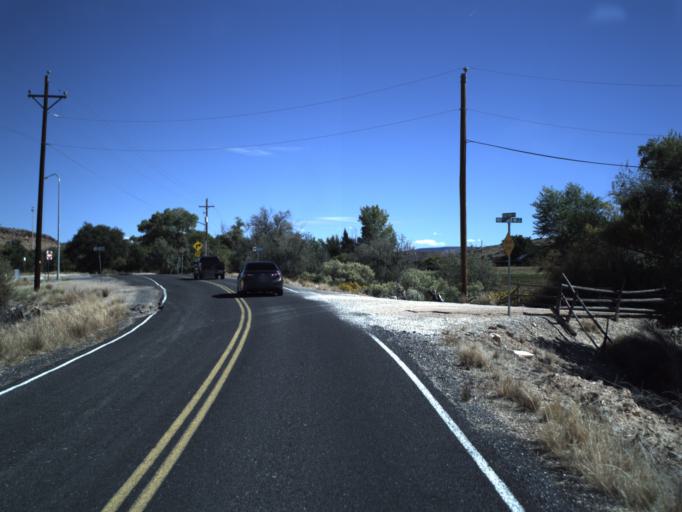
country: US
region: Utah
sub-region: Washington County
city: Toquerville
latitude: 37.2279
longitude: -113.3743
